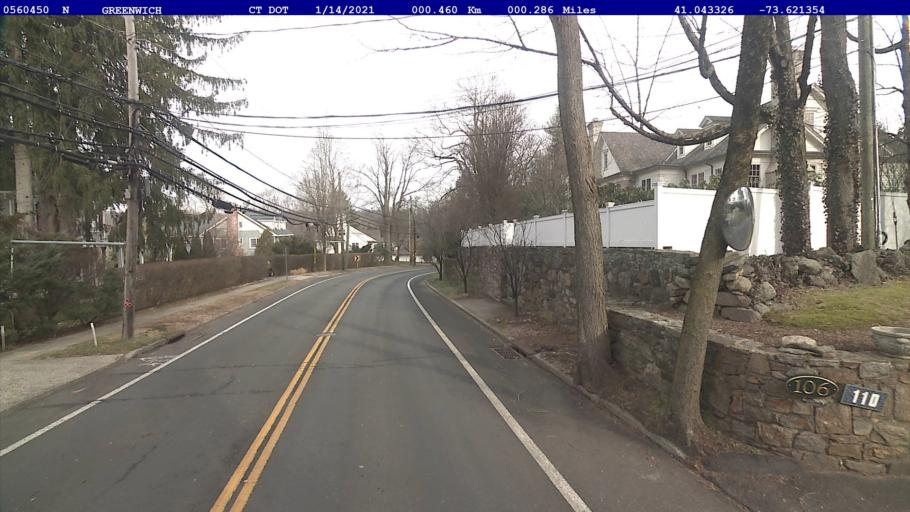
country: US
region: Connecticut
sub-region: Fairfield County
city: Greenwich
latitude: 41.0433
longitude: -73.6213
